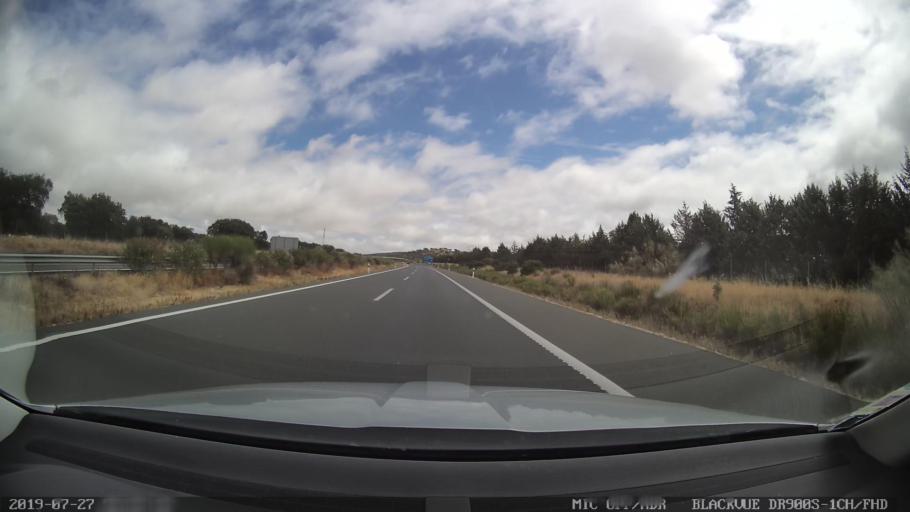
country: ES
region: Extremadura
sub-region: Provincia de Caceres
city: Almaraz
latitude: 39.7953
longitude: -5.6825
